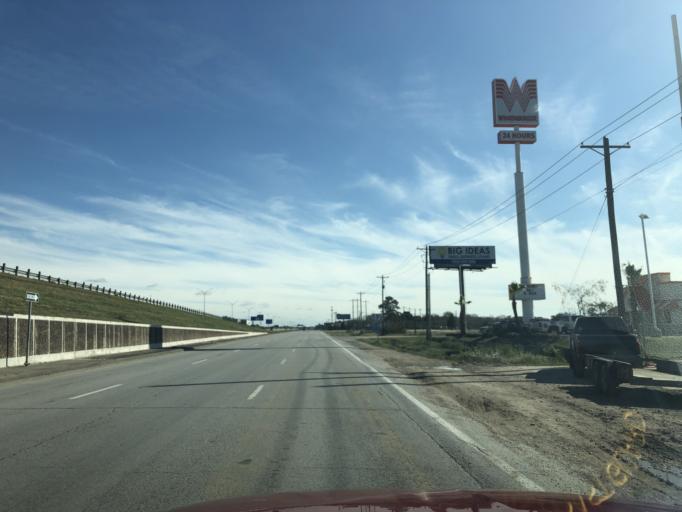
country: US
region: Texas
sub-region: Galveston County
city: Hitchcock
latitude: 29.4019
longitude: -95.0329
